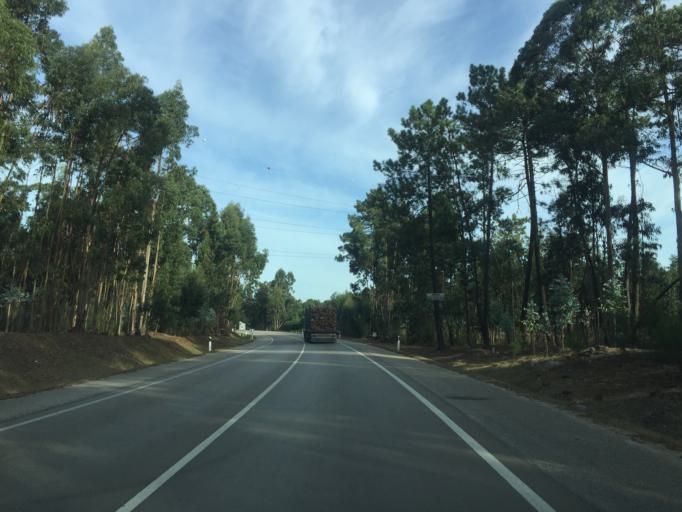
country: PT
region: Leiria
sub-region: Pombal
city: Lourical
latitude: 40.0121
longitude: -8.8072
